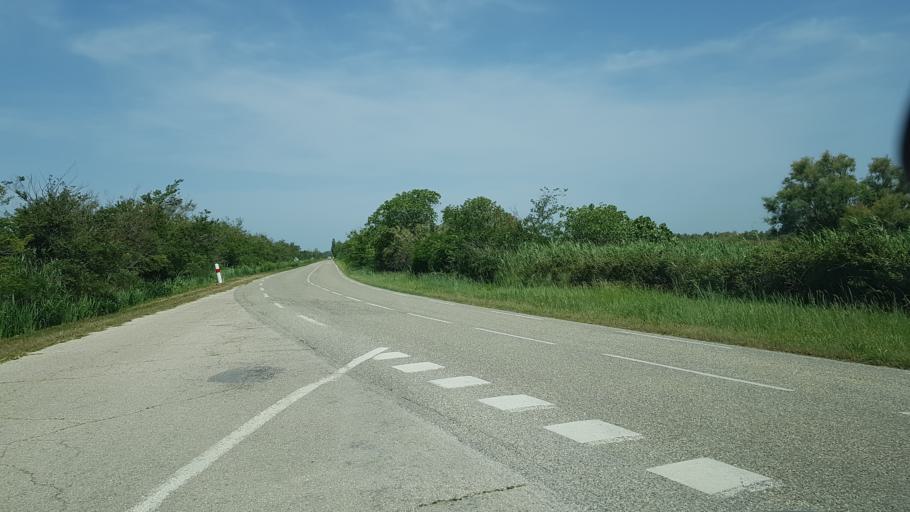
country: FR
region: Languedoc-Roussillon
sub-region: Departement du Gard
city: Saint-Gilles
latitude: 43.5811
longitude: 4.5034
